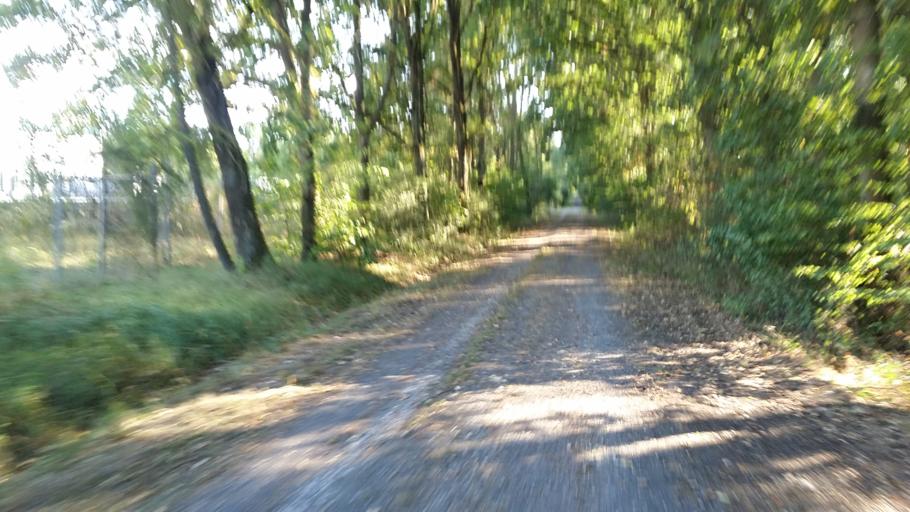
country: DE
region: Hesse
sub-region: Regierungsbezirk Giessen
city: Giessen
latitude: 50.5782
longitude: 8.7244
